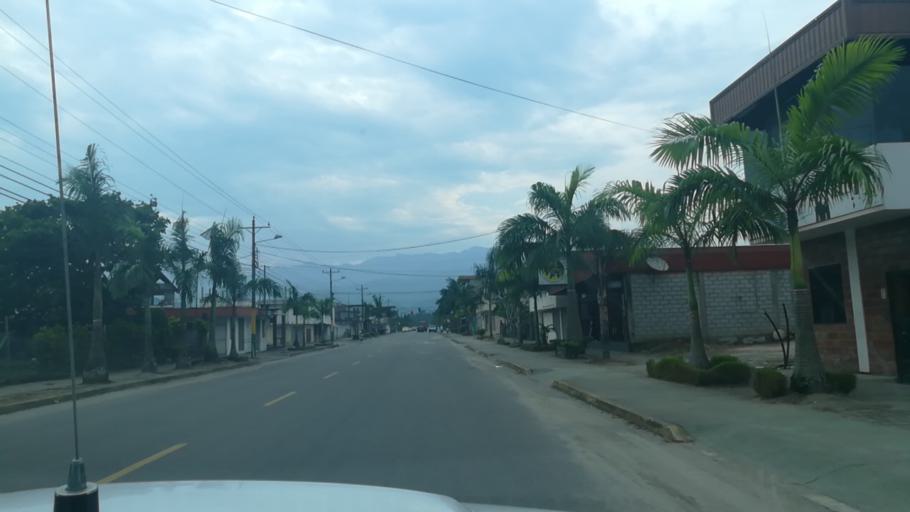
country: EC
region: Napo
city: Tena
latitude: -0.9855
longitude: -77.8176
